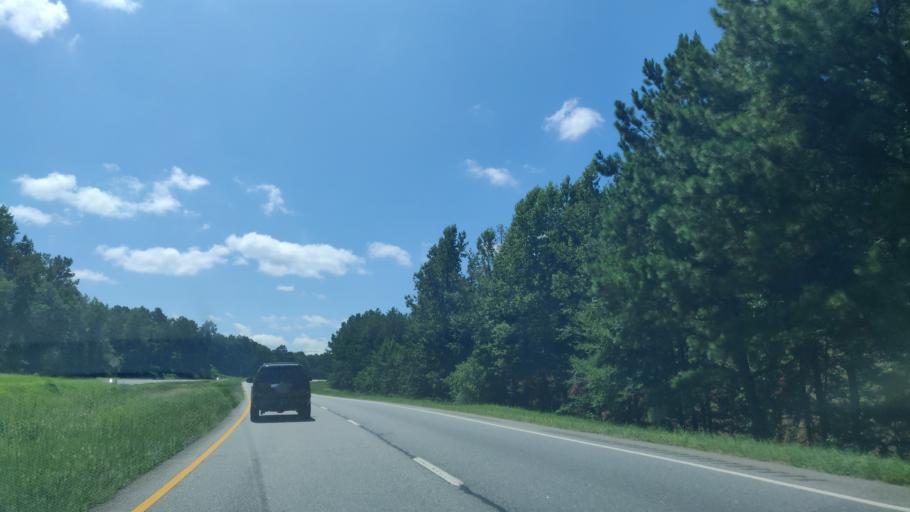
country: US
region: Georgia
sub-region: Chattahoochee County
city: Cusseta
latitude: 32.2424
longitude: -84.7172
